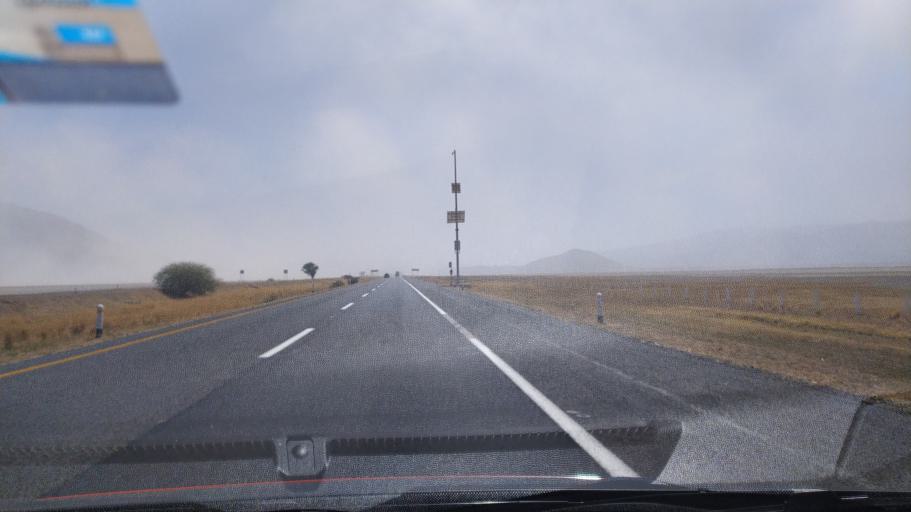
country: MX
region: Jalisco
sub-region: Acatlan de Juarez
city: Villa de los Ninos
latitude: 20.3246
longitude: -103.5668
